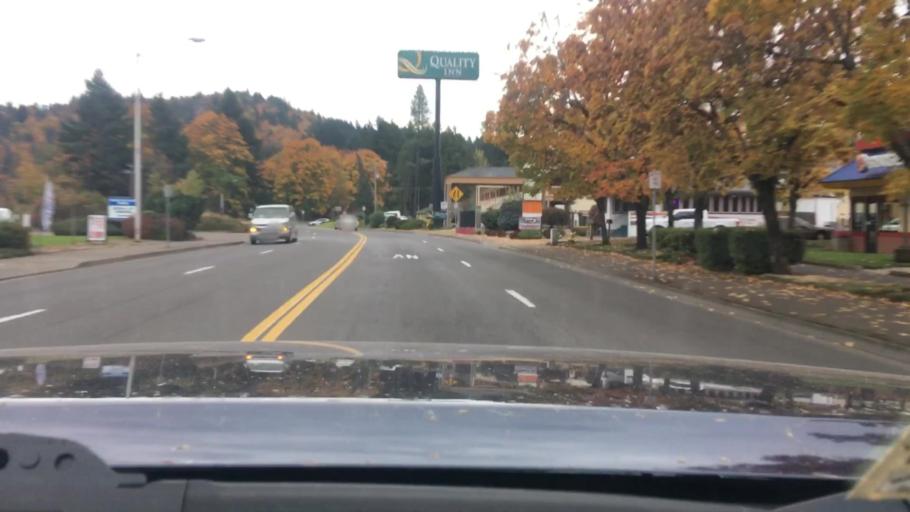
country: US
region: Oregon
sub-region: Lane County
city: Cottage Grove
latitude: 43.8028
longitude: -123.0454
